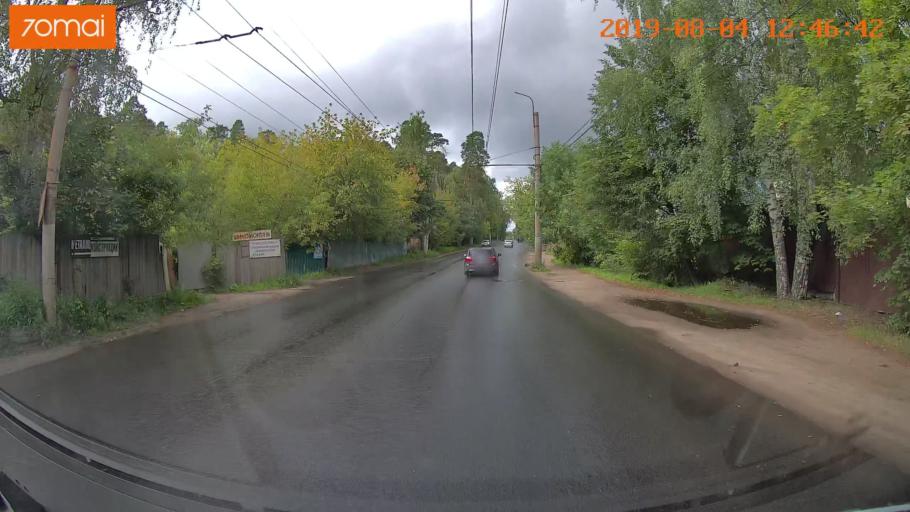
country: RU
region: Ivanovo
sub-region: Gorod Ivanovo
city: Ivanovo
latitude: 57.0231
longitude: 40.9454
